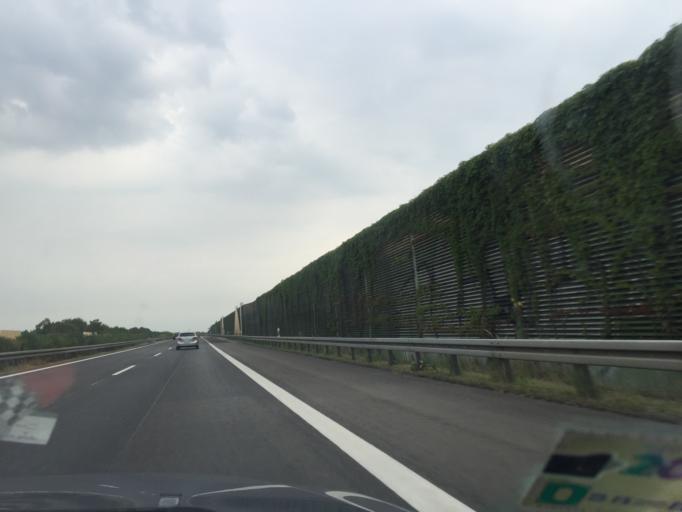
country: DE
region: Brandenburg
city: Bernau bei Berlin
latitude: 52.6745
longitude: 13.5658
